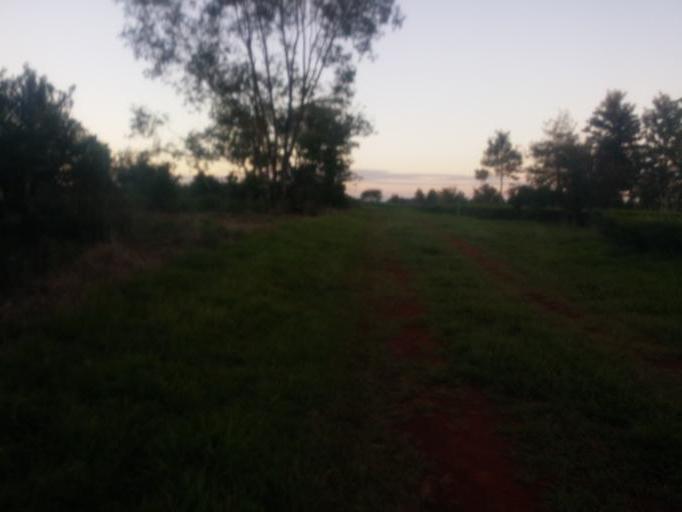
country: AR
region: Misiones
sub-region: Departamento de Obera
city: Obera
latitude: -27.4456
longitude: -55.0920
